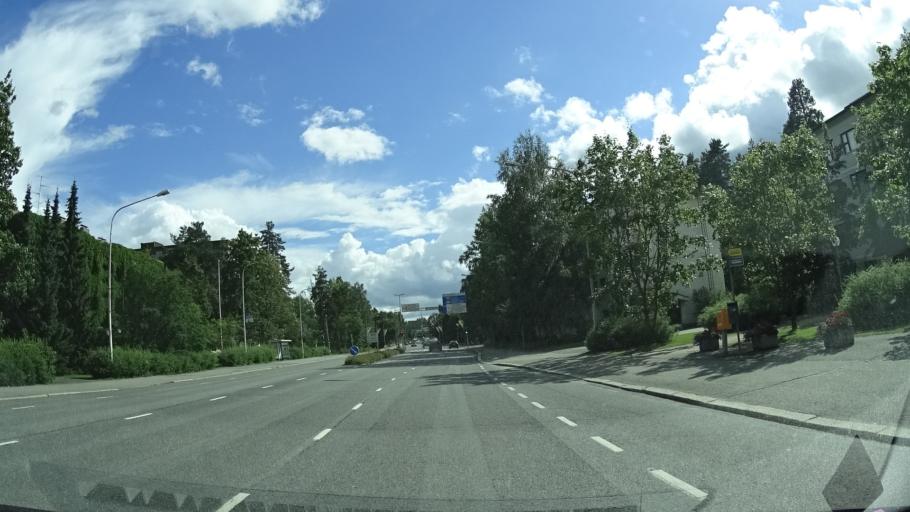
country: FI
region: Pirkanmaa
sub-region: Etelae-Pirkanmaa
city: Valkeakoski
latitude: 61.2722
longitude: 24.0210
